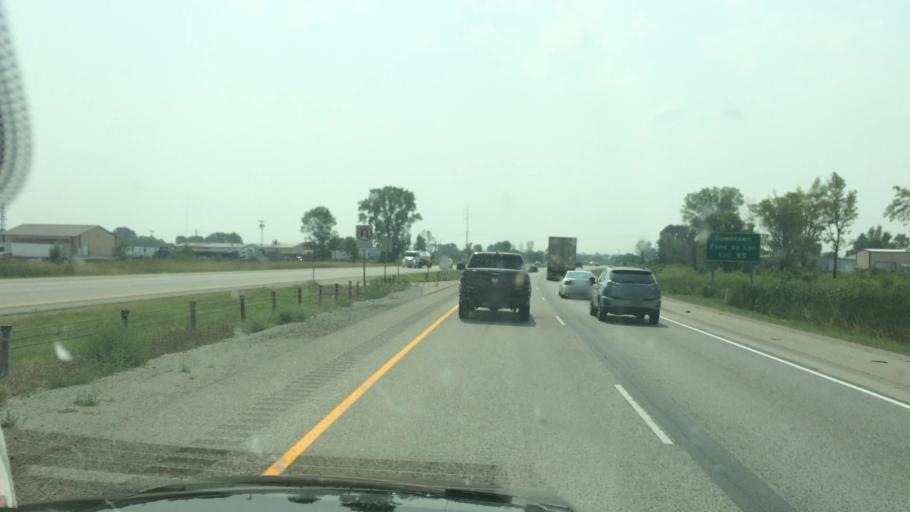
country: US
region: Wisconsin
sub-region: Fond du Lac County
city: North Fond du Lac
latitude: 43.7984
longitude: -88.4875
